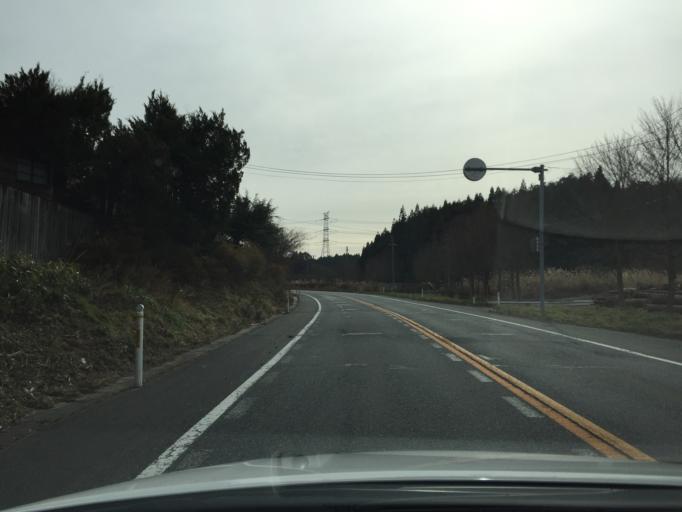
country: JP
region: Fukushima
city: Ishikawa
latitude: 37.2029
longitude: 140.6109
